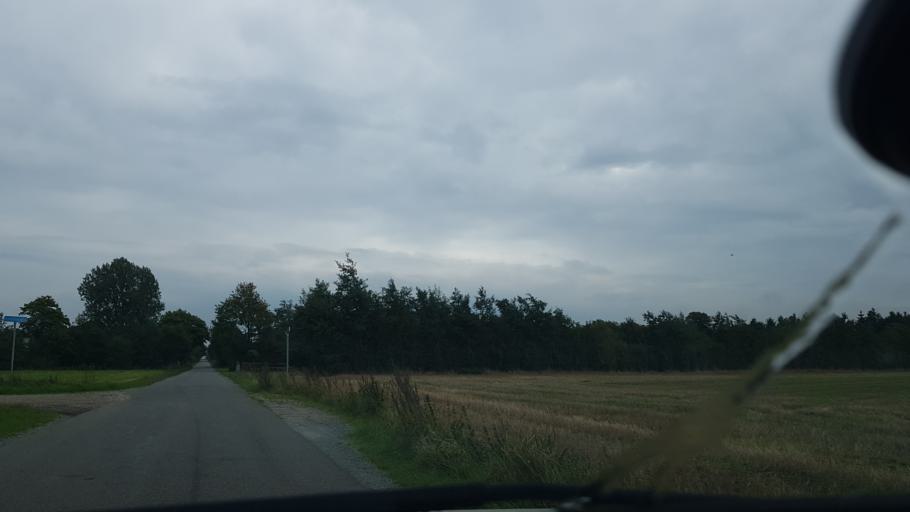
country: DK
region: South Denmark
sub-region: Vejle Kommune
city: Egtved
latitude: 55.5846
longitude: 9.2170
